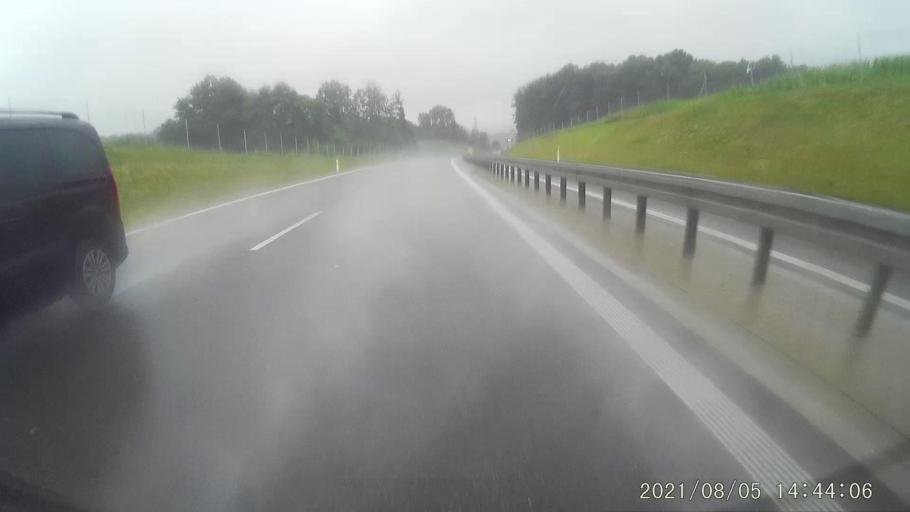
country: PL
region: Opole Voivodeship
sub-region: Powiat nyski
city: Nysa
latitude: 50.4914
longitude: 17.3839
